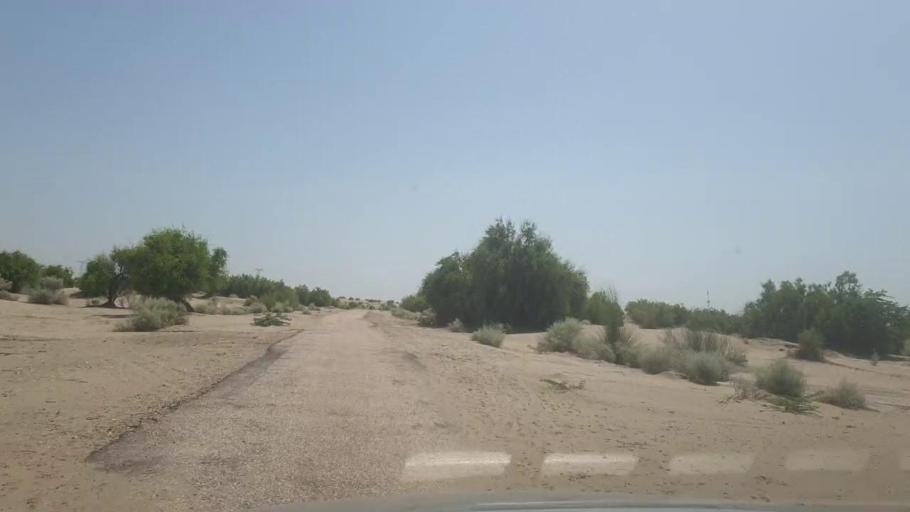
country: PK
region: Sindh
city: Khairpur
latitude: 27.3535
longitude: 69.0748
